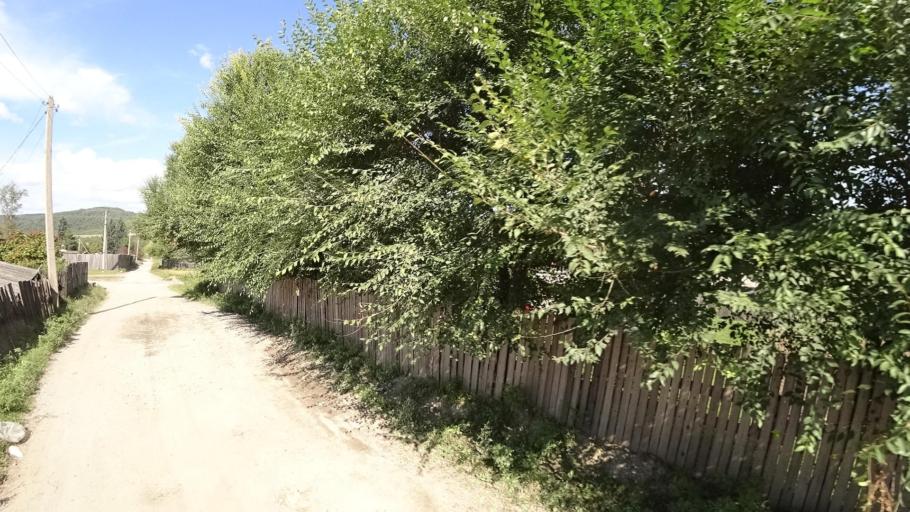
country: RU
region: Jewish Autonomous Oblast
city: Londoko
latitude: 49.0141
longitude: 131.8726
